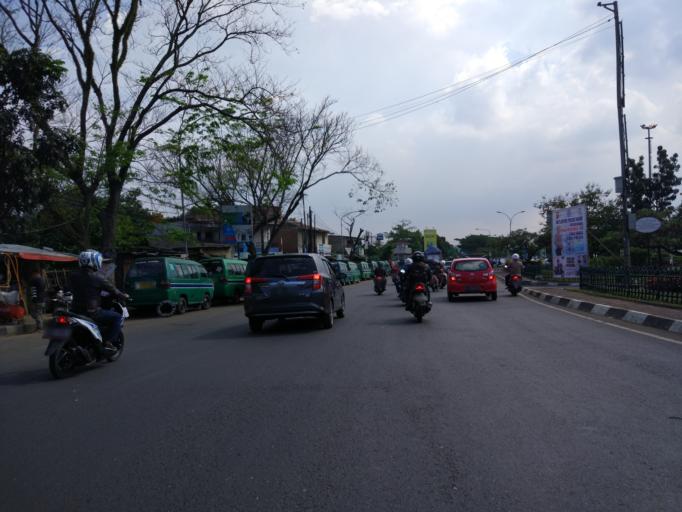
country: ID
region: West Java
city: Cileunyi
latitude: -6.9352
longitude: 107.7185
